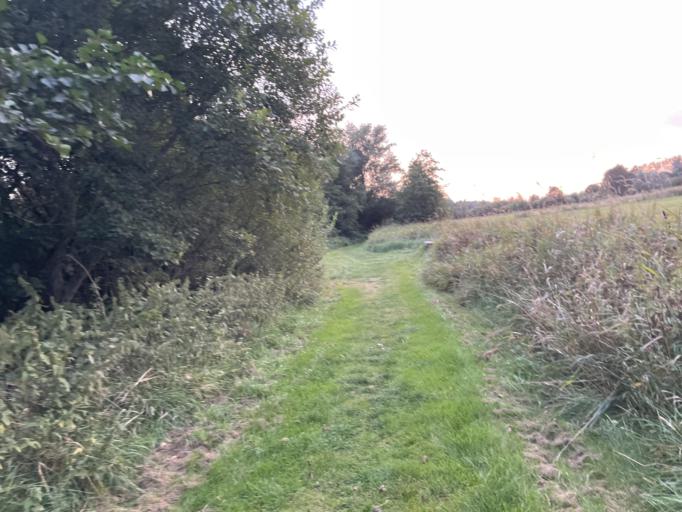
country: DE
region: Schleswig-Holstein
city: Mildstedt
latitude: 54.4753
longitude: 9.1117
